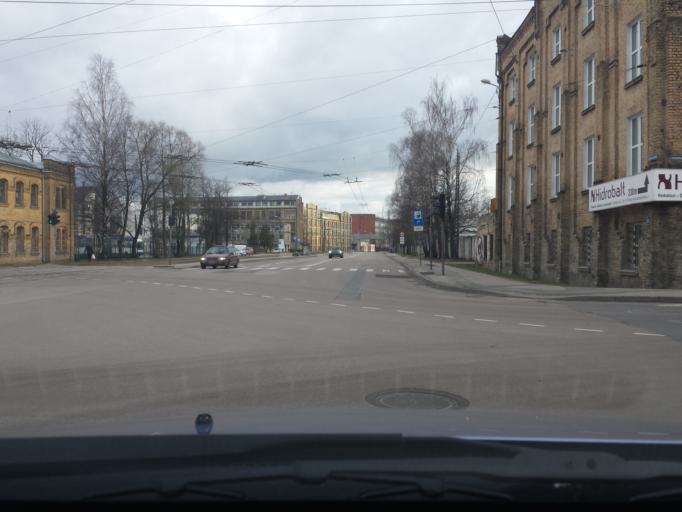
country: LV
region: Riga
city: Riga
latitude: 56.9887
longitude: 24.1216
